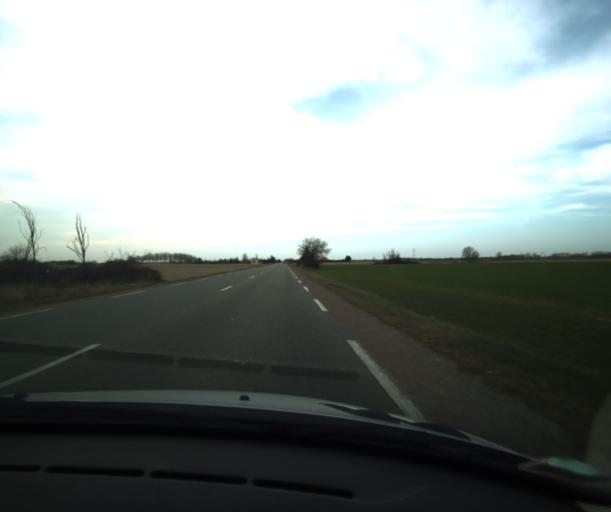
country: FR
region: Midi-Pyrenees
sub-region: Departement du Tarn-et-Garonne
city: Montech
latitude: 43.9679
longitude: 1.2069
